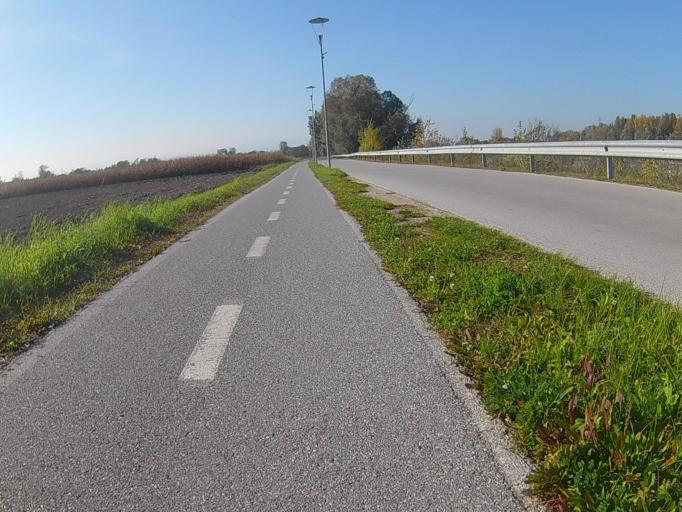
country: SI
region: Hajdina
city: Spodnja Hajdina
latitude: 46.4260
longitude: 15.8485
